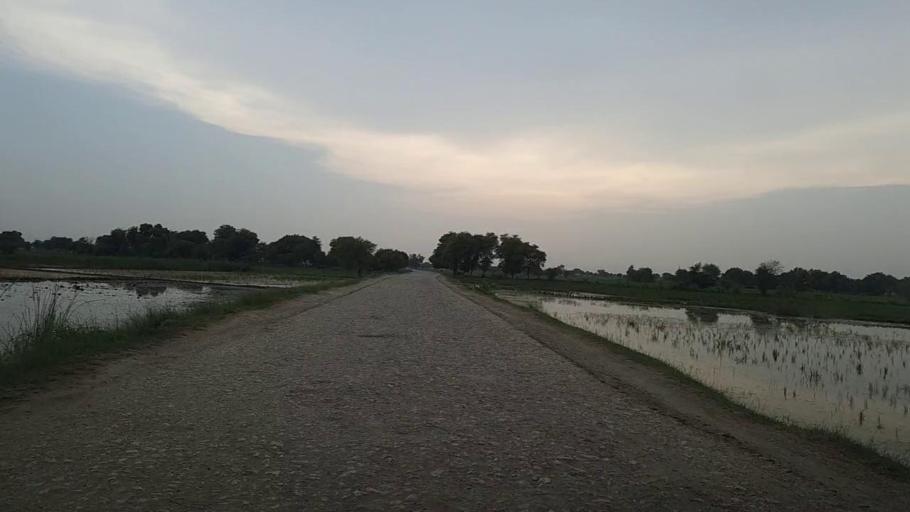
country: PK
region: Sindh
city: Khanpur
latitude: 27.8484
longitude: 69.4345
